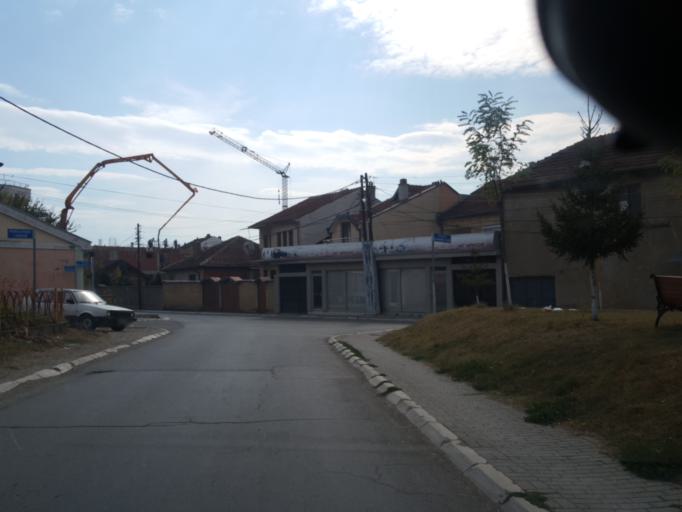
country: XK
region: Gjakova
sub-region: Komuna e Gjakoves
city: Gjakove
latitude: 42.3744
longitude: 20.4298
